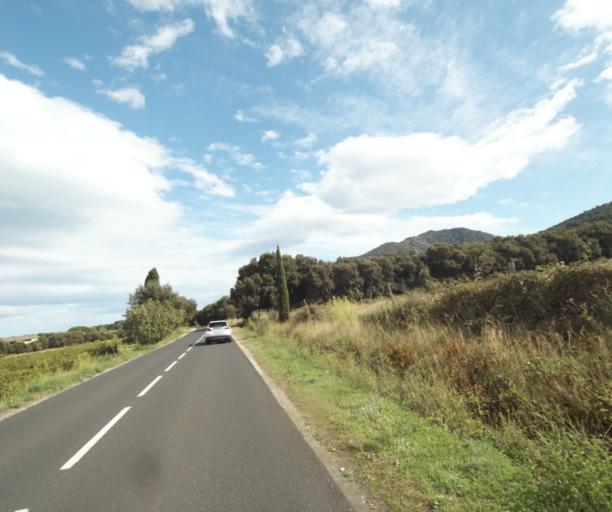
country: FR
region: Languedoc-Roussillon
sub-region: Departement des Pyrenees-Orientales
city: Sorede
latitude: 42.5312
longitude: 2.9746
